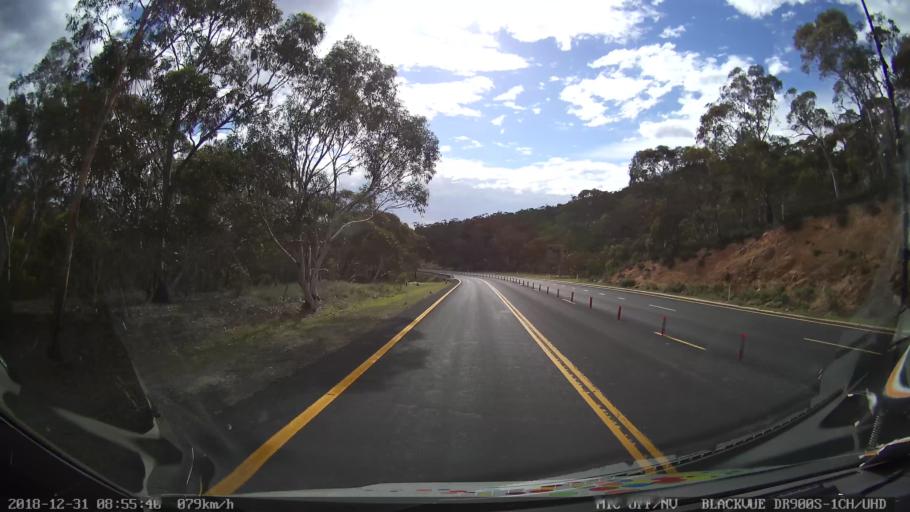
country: AU
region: New South Wales
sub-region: Snowy River
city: Jindabyne
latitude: -36.3449
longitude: 148.5705
